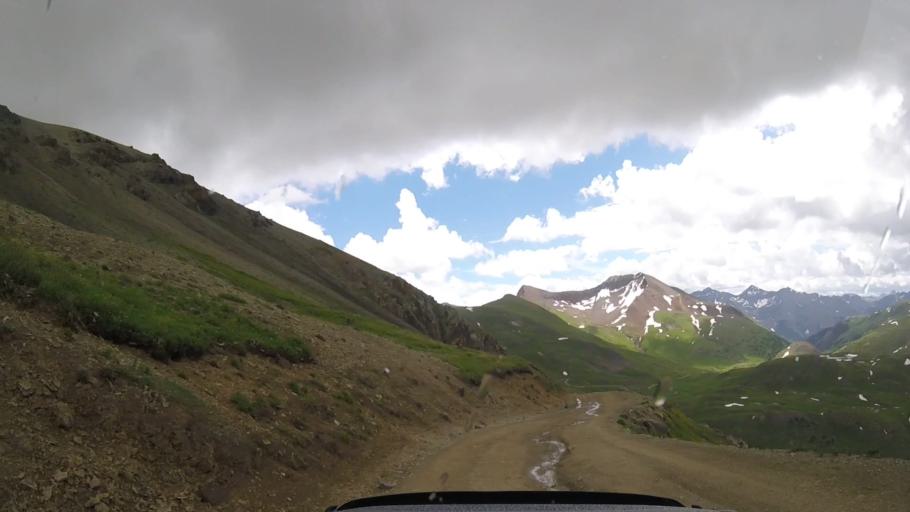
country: US
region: Colorado
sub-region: Ouray County
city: Ouray
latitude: 37.9668
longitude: -107.5863
